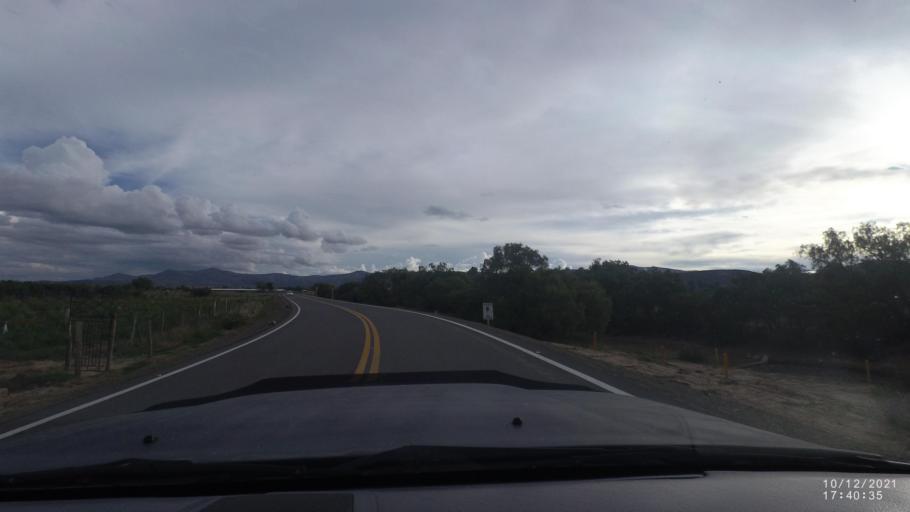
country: BO
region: Cochabamba
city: Tarata
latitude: -17.5877
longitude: -66.0203
